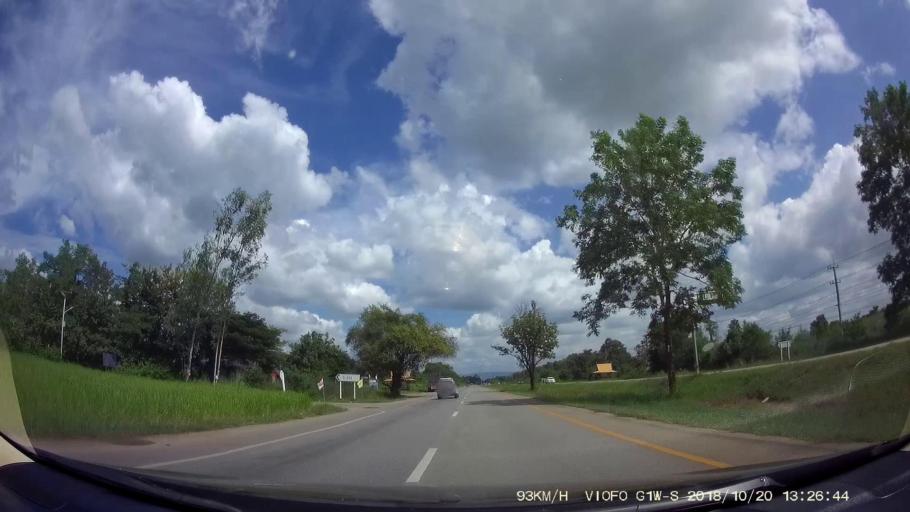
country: TH
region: Chaiyaphum
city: Khon San
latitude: 16.5934
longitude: 101.9506
